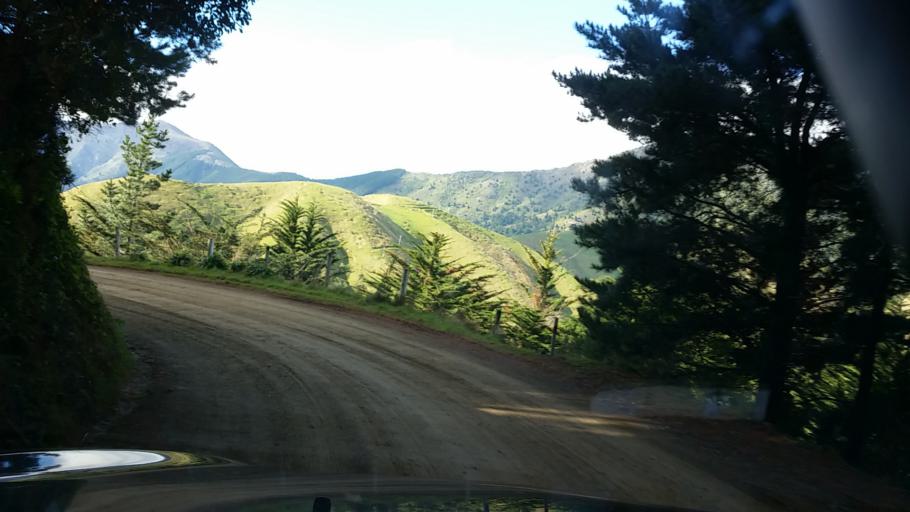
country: NZ
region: Marlborough
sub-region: Marlborough District
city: Picton
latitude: -40.9854
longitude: 173.8265
